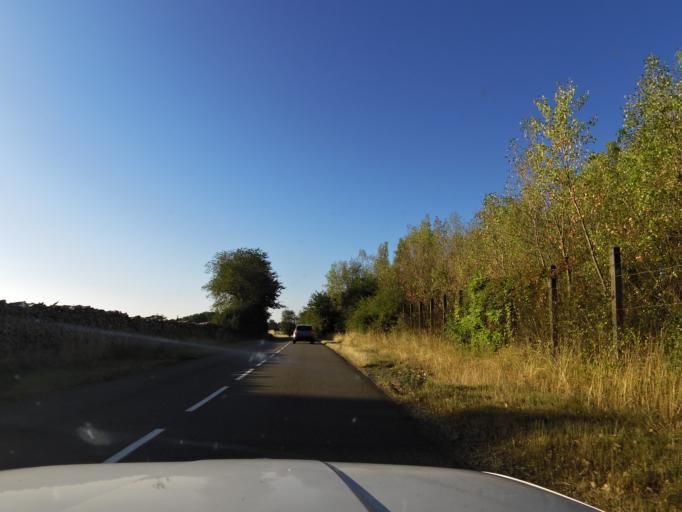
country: FR
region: Rhone-Alpes
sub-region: Departement de l'Ain
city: Meximieux
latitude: 45.8827
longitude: 5.2150
